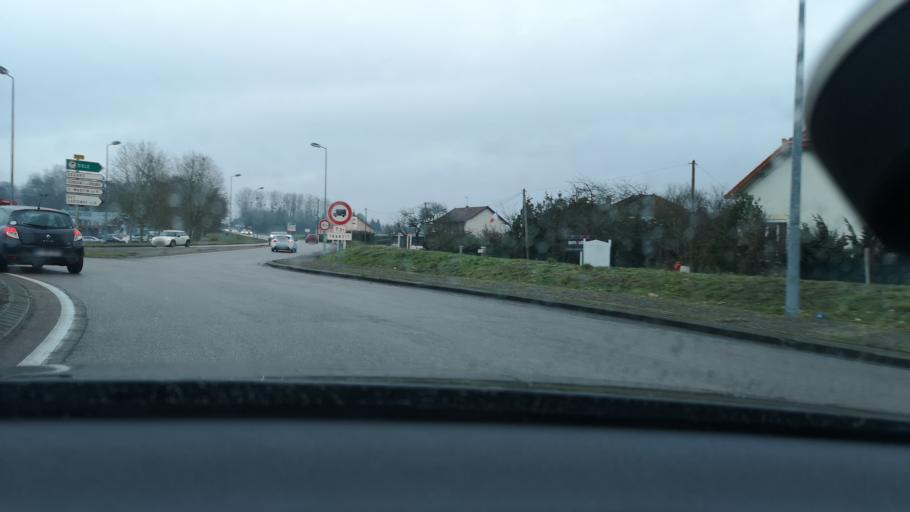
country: FR
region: Bourgogne
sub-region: Departement de Saone-et-Loire
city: Saint-Marcel
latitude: 46.7846
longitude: 4.9092
